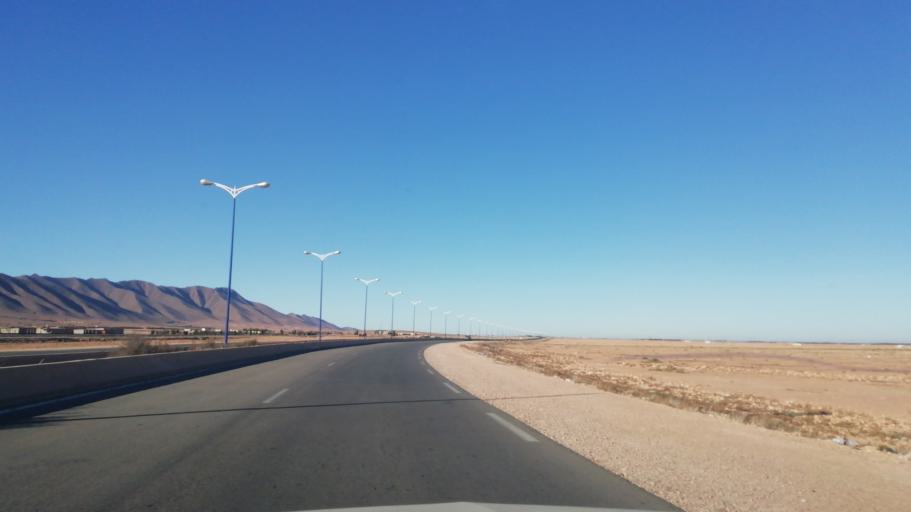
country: DZ
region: Wilaya de Naama
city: Naama
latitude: 33.5679
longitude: -0.2404
